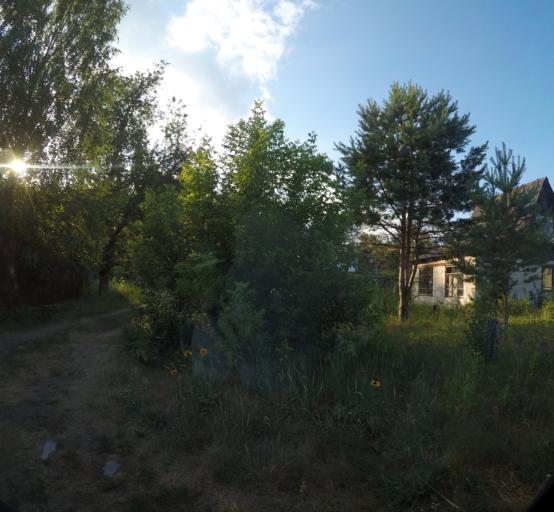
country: LT
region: Alytaus apskritis
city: Druskininkai
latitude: 53.9208
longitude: 24.1894
